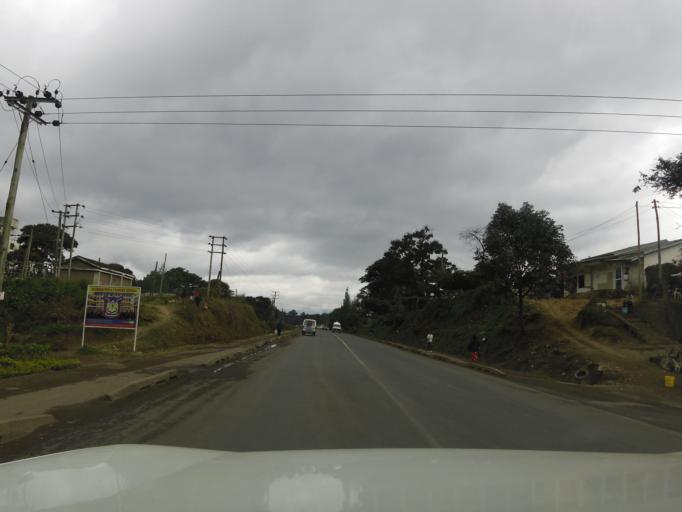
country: TZ
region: Arusha
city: Arusha
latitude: -3.3635
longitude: 36.7021
